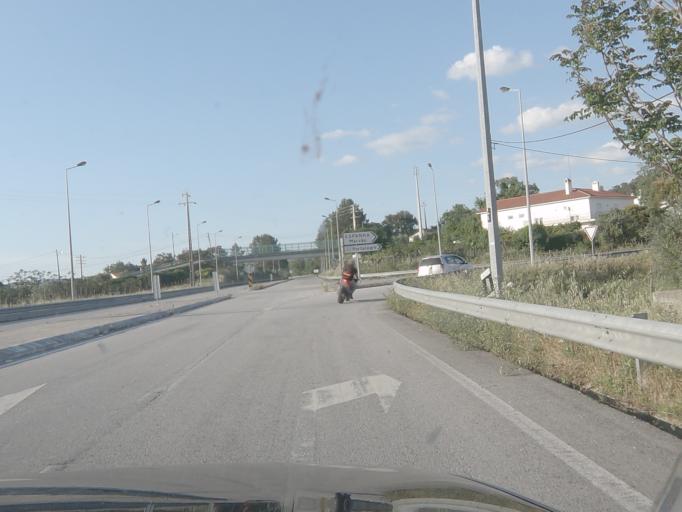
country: PT
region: Portalegre
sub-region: Portalegre
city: Portalegre
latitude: 39.3107
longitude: -7.4430
